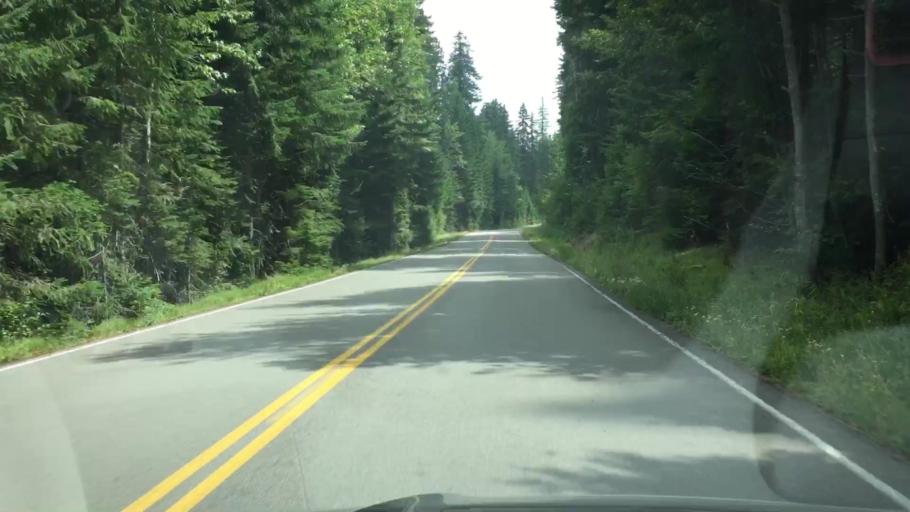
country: US
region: Washington
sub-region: Klickitat County
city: White Salmon
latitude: 46.1311
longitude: -121.6299
